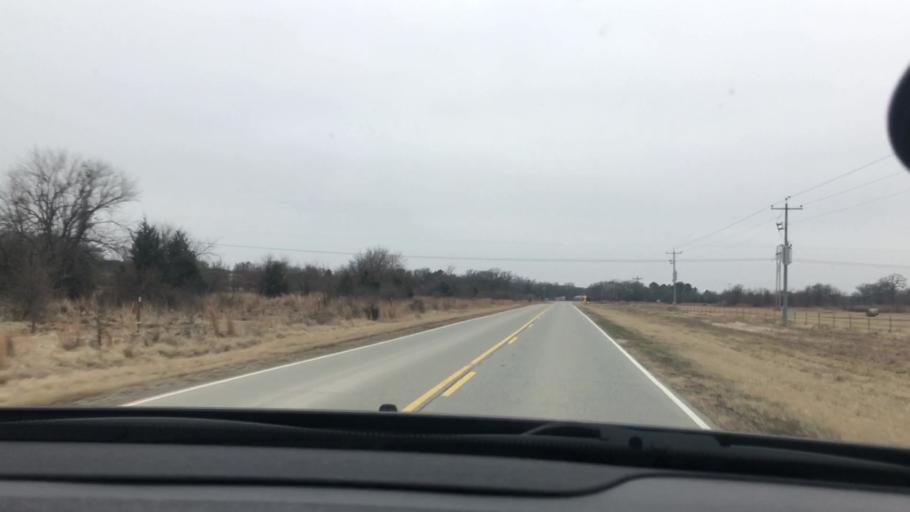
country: US
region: Oklahoma
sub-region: Coal County
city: Coalgate
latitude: 34.5082
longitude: -96.2979
